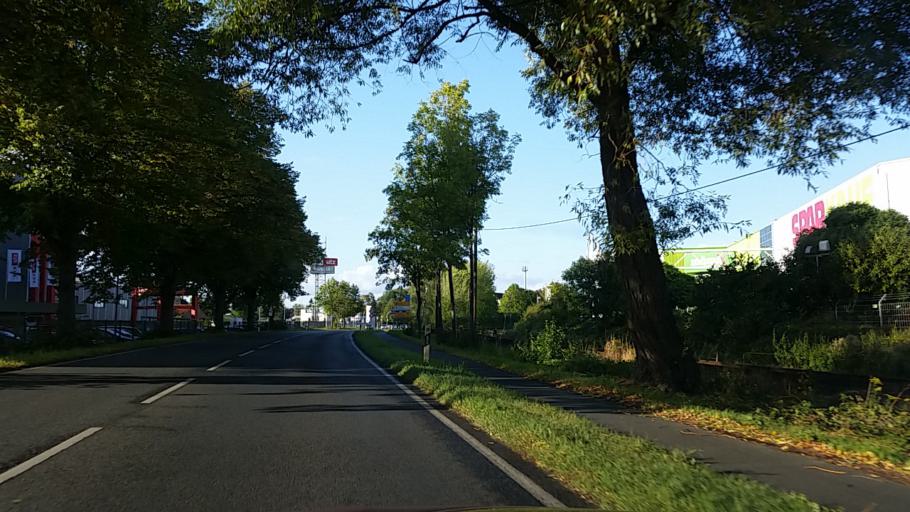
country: DE
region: Lower Saxony
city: Vordorf
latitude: 52.3282
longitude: 10.5221
